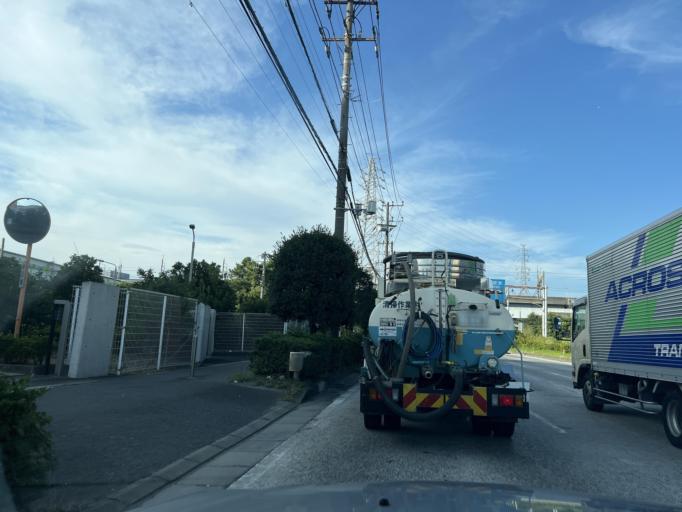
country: JP
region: Chiba
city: Funabashi
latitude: 35.6901
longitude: 139.9618
